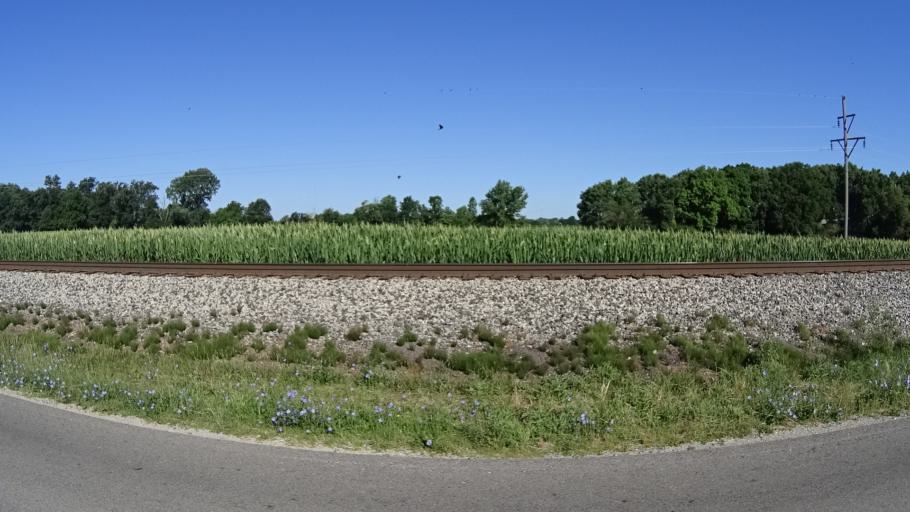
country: US
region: Ohio
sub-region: Erie County
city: Sandusky
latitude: 41.3926
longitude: -82.7550
